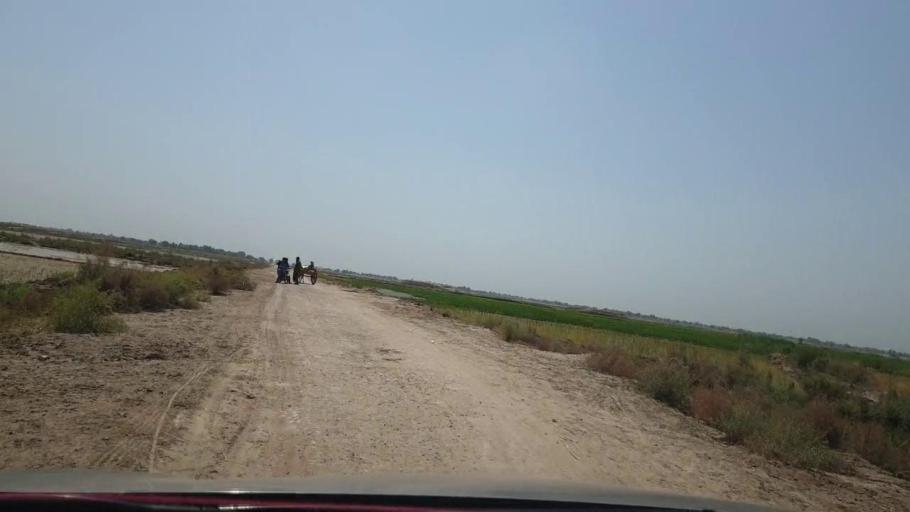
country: PK
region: Sindh
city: Kambar
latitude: 27.5815
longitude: 67.8773
